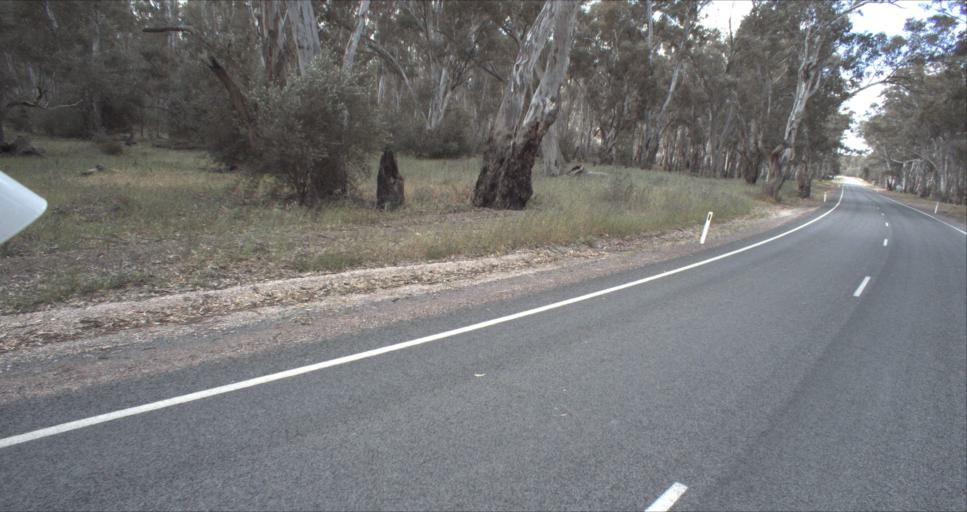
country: AU
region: New South Wales
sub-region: Leeton
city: Leeton
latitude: -34.6411
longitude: 146.3684
